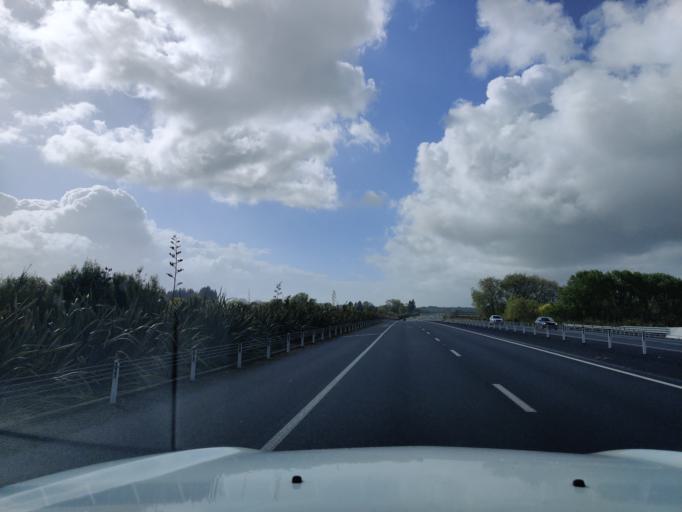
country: NZ
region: Waikato
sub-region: Waipa District
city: Cambridge
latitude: -37.8461
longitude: 175.3795
